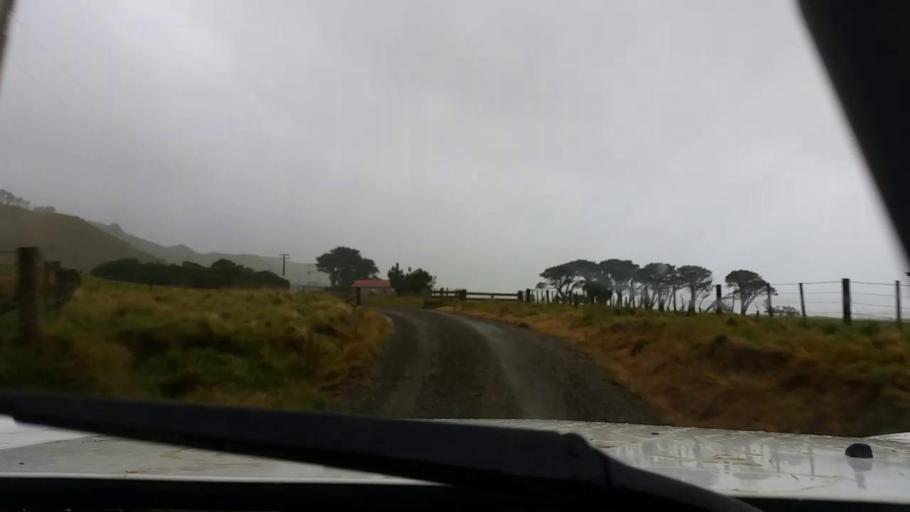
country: NZ
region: Wellington
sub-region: Masterton District
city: Masterton
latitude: -41.2637
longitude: 175.8930
